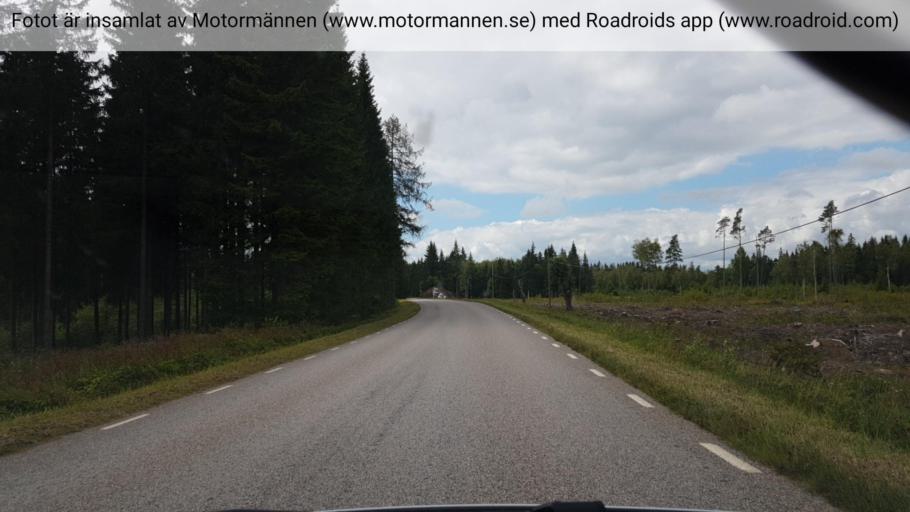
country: SE
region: Vaestra Goetaland
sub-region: Ulricehamns Kommun
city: Ulricehamn
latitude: 57.8030
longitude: 13.5631
